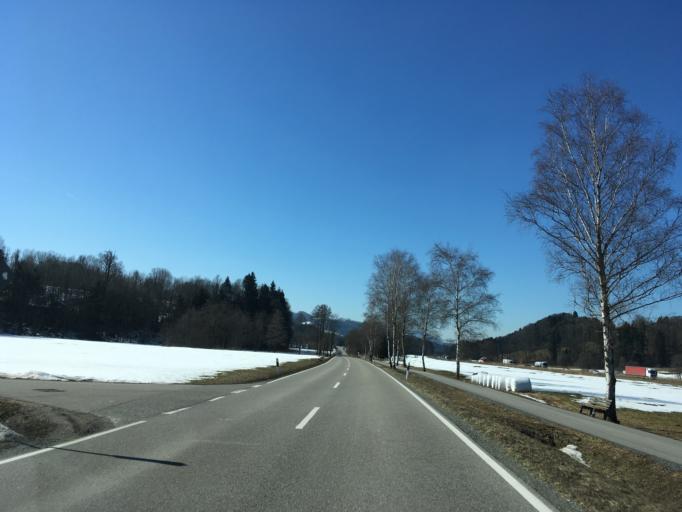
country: DE
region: Bavaria
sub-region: Upper Bavaria
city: Frasdorf
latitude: 47.8005
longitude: 12.2690
